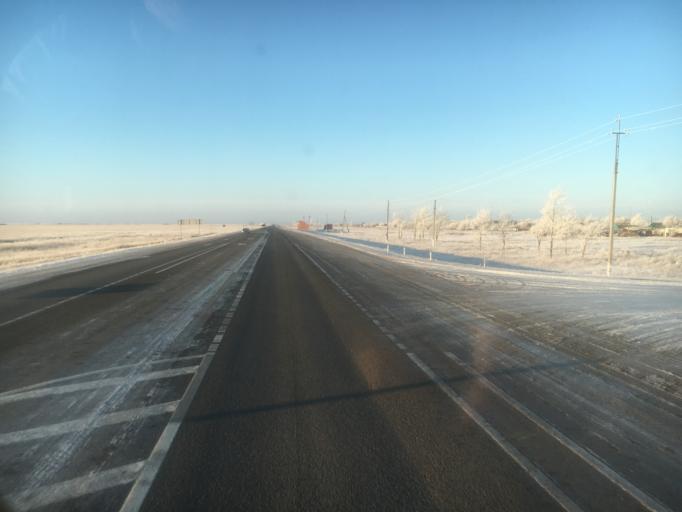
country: KZ
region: Soltustik Qazaqstan
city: Taiynsha
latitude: 53.8927
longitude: 69.2649
